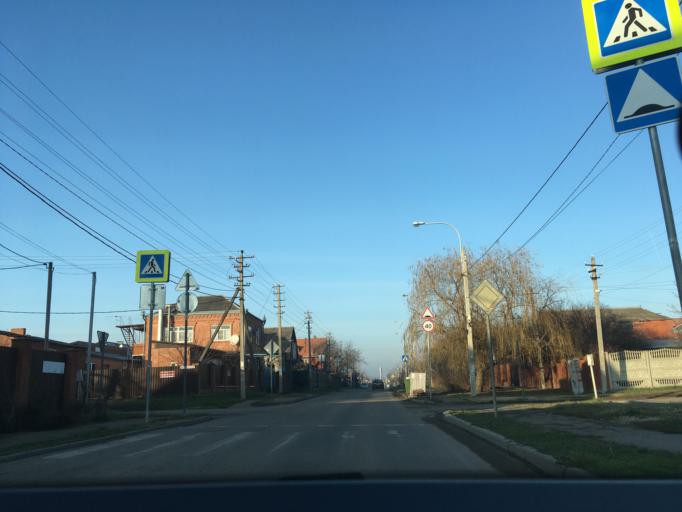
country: RU
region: Krasnodarskiy
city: Krasnodar
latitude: 45.1194
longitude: 39.0144
